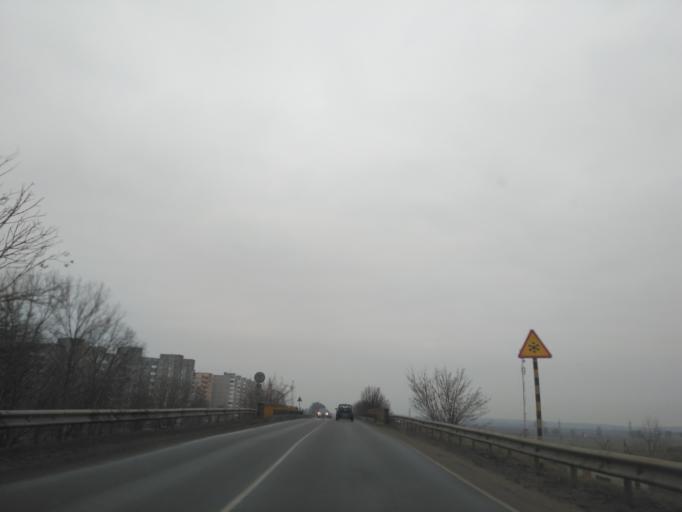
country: BY
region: Brest
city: Baranovichi
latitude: 53.1598
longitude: 26.0086
